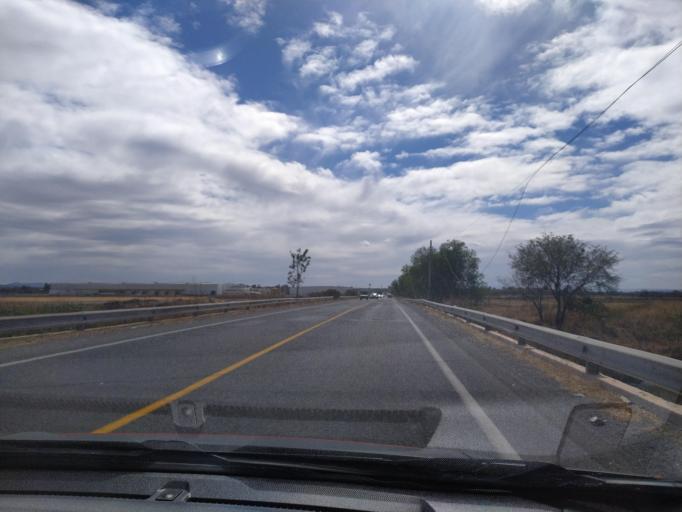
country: LA
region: Oudomxai
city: Muang La
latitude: 21.0092
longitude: 101.8294
